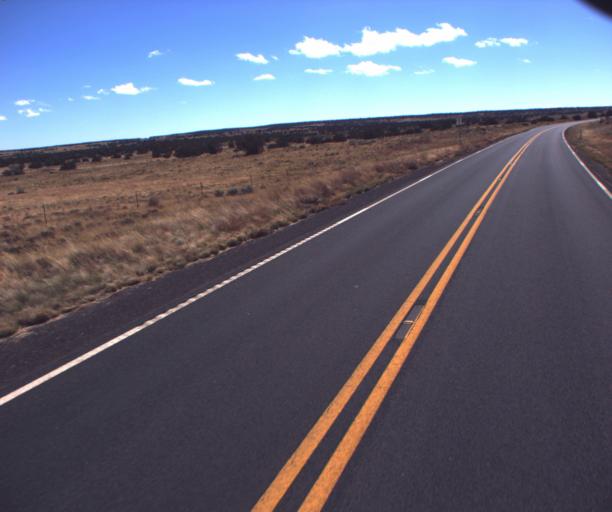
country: US
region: Arizona
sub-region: Apache County
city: Houck
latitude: 35.0058
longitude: -109.2292
